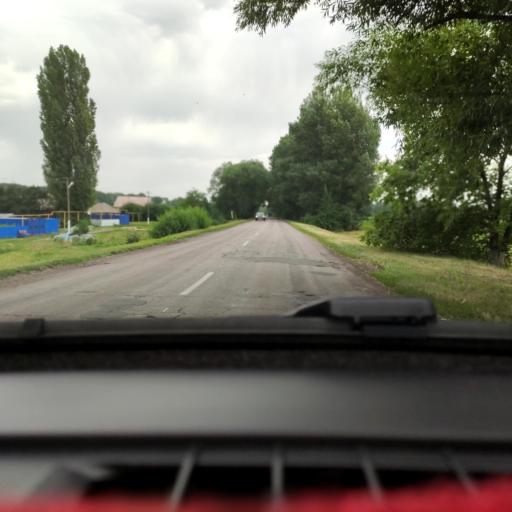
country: RU
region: Voronezj
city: Davydovka
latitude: 51.2456
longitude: 39.5699
